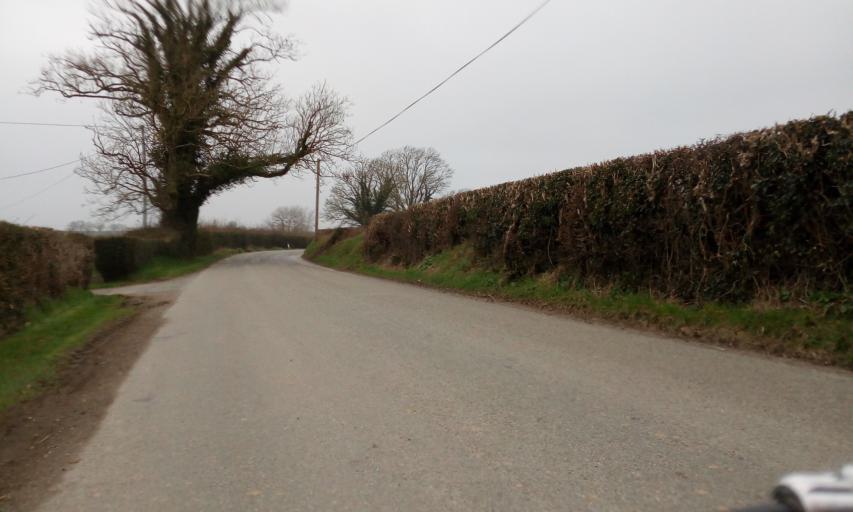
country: IE
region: Leinster
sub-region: Kilkenny
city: Kilkenny
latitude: 52.6579
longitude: -7.1840
